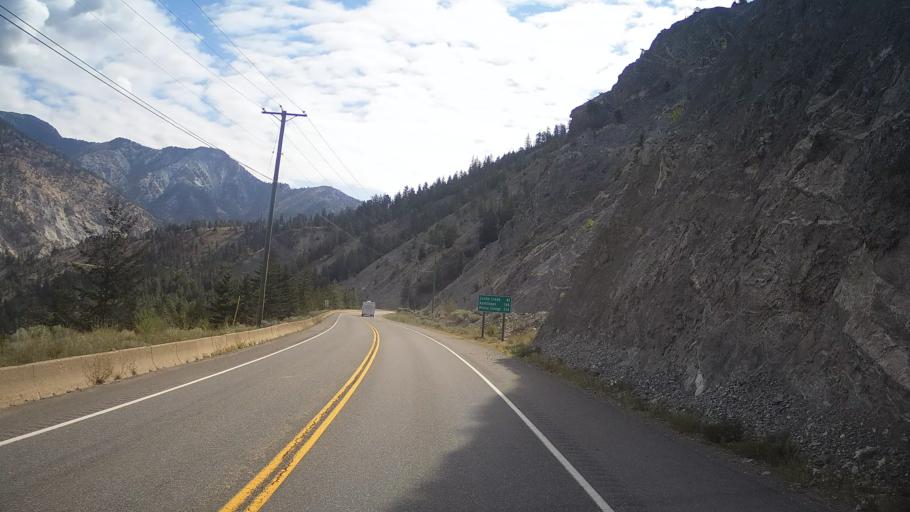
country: CA
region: British Columbia
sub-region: Thompson-Nicola Regional District
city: Ashcroft
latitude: 50.2496
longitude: -121.5557
